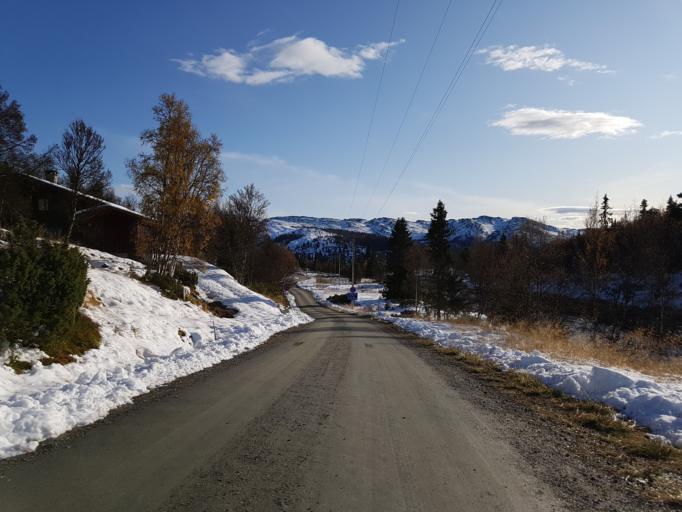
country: NO
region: Oppland
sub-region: Sel
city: Otta
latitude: 61.8192
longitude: 9.6775
